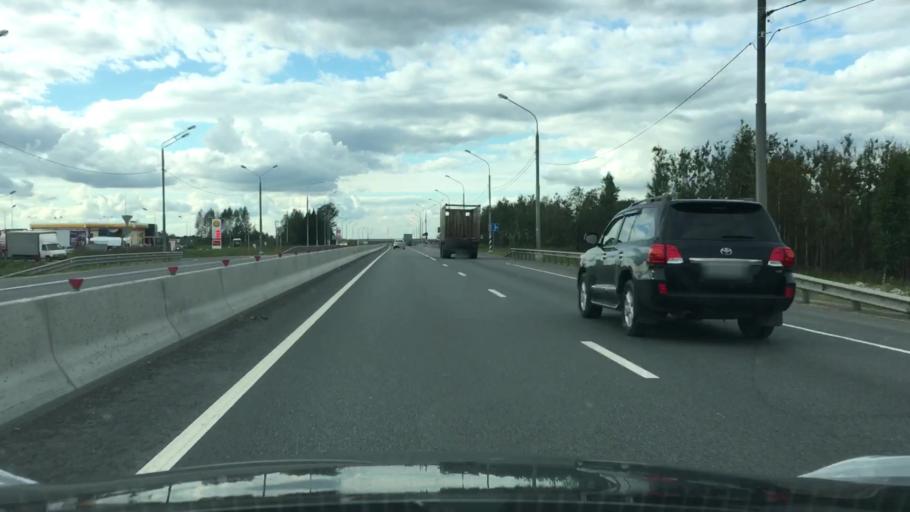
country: RU
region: Tverskaya
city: Tver
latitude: 56.7851
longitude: 35.9322
